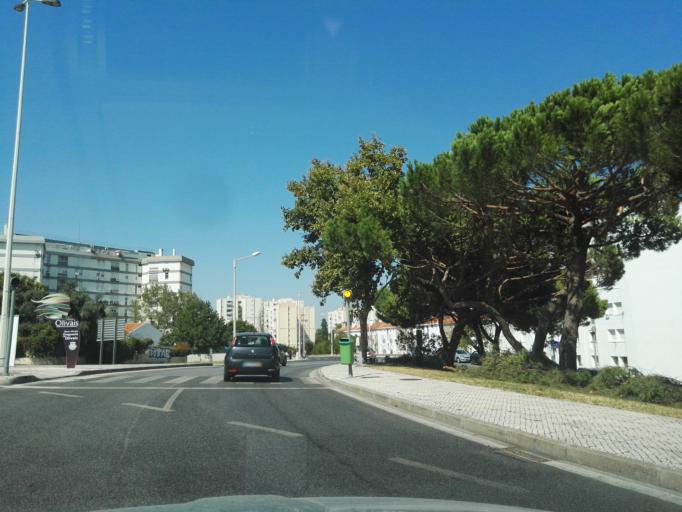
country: PT
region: Lisbon
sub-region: Loures
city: Moscavide
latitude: 38.7587
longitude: -9.1117
